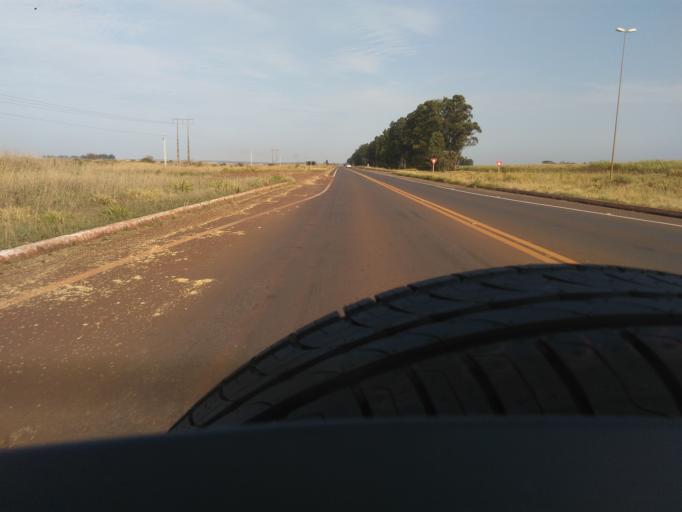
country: BR
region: Mato Grosso do Sul
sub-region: Dourados
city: Dourados
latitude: -22.3020
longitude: -55.1031
